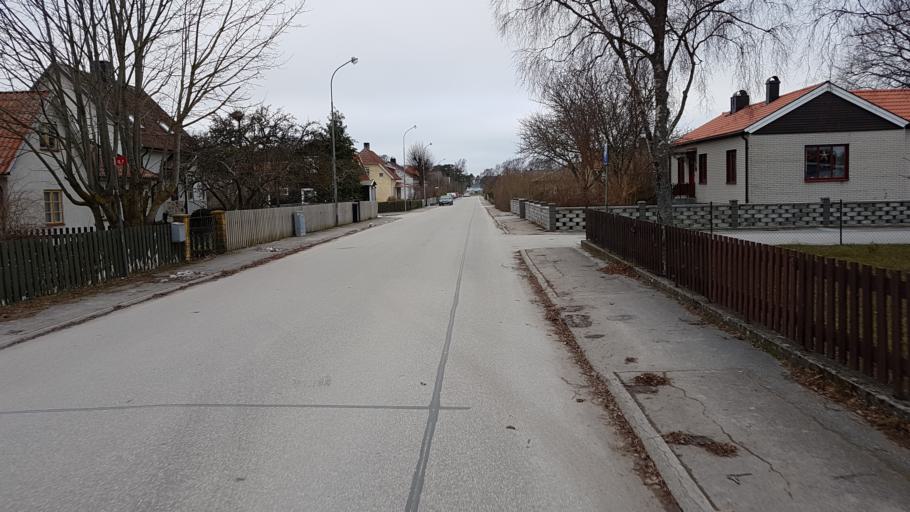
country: SE
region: Gotland
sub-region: Gotland
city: Visby
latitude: 57.6224
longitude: 18.3052
